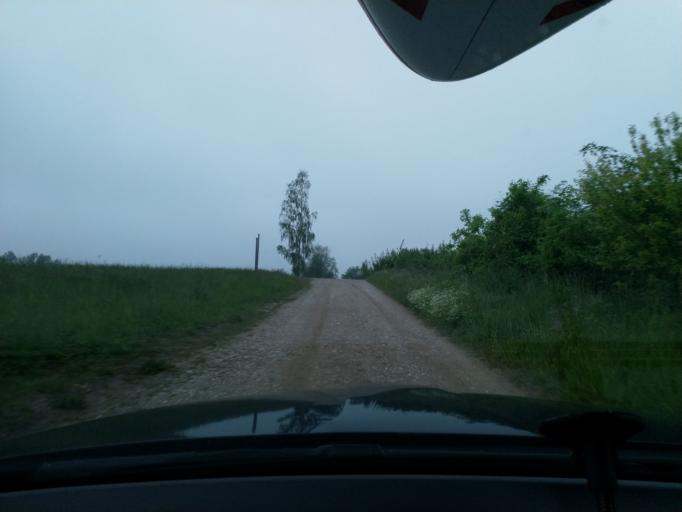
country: LV
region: Kuldigas Rajons
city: Kuldiga
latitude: 56.8783
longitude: 21.8252
